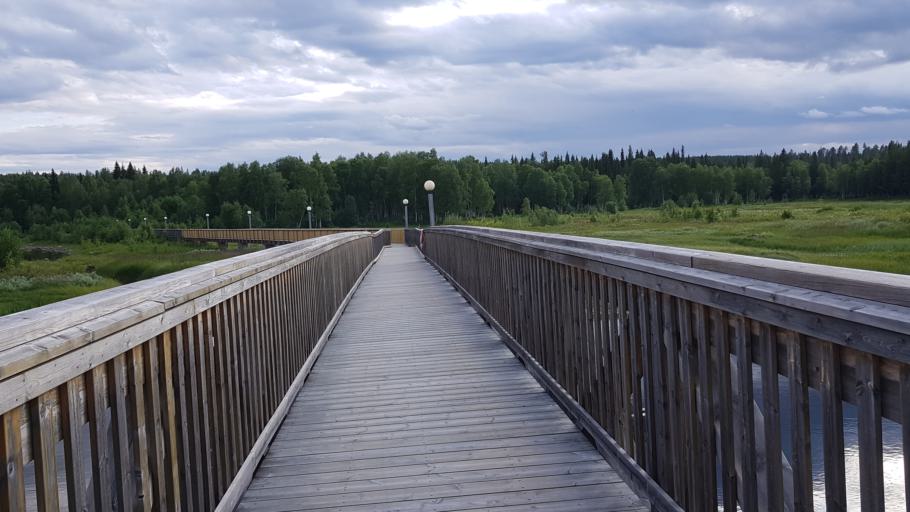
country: SE
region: Norrbotten
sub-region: Alvsbyns Kommun
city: AElvsbyn
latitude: 65.8567
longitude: 20.4185
